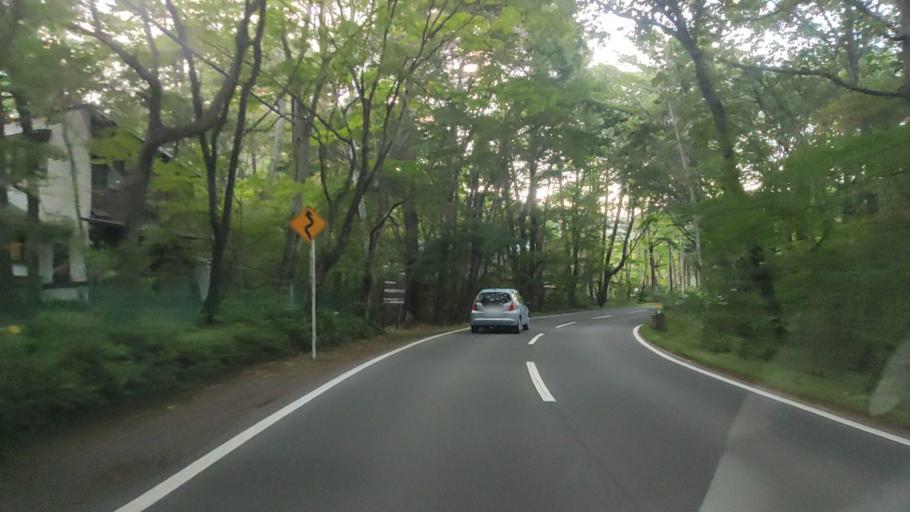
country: JP
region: Nagano
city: Komoro
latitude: 36.3761
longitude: 138.5873
